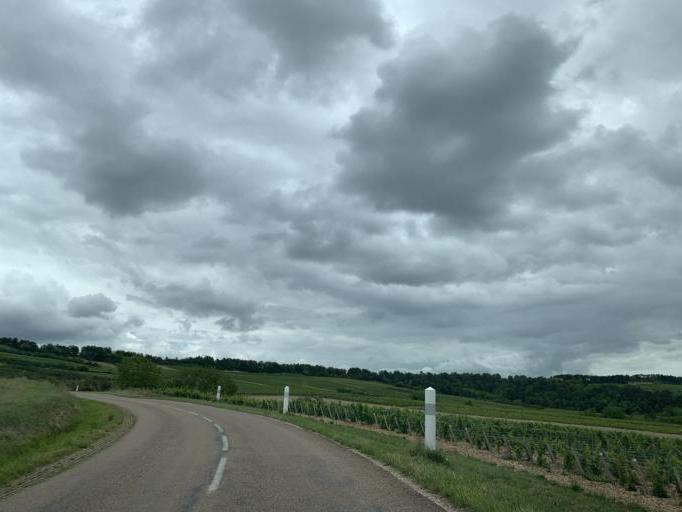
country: FR
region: Bourgogne
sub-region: Departement de l'Yonne
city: Saint-Bris-le-Vineux
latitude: 47.7173
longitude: 3.6741
